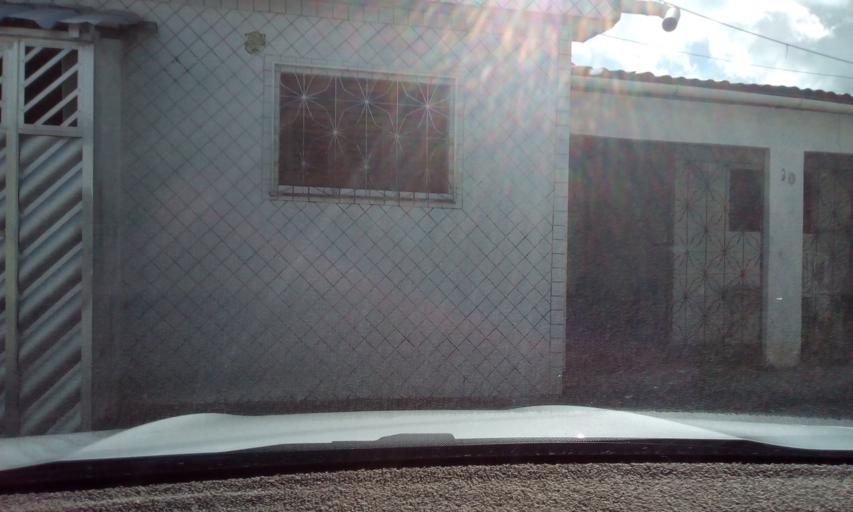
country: BR
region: Paraiba
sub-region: Bayeux
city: Bayeux
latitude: -7.1222
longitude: -34.9193
